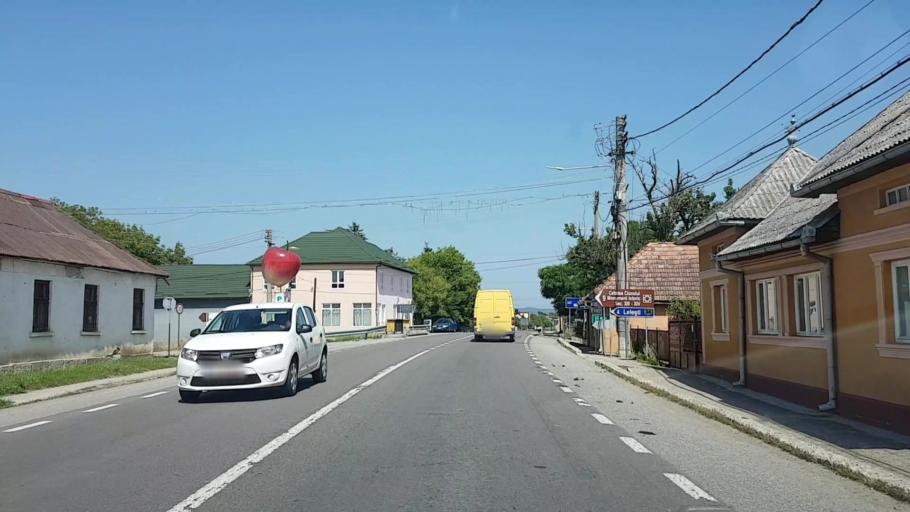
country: RO
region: Bistrita-Nasaud
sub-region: Comuna Ciceu-Mihaiesti
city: Ciceu-Mihaiesti
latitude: 47.1852
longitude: 23.9721
